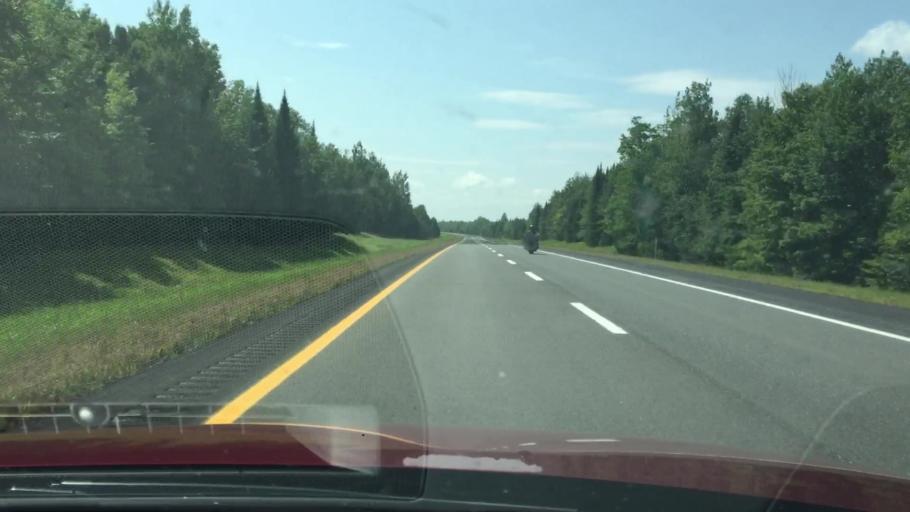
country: US
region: Maine
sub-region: Penobscot County
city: Patten
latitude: 45.9613
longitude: -68.3167
